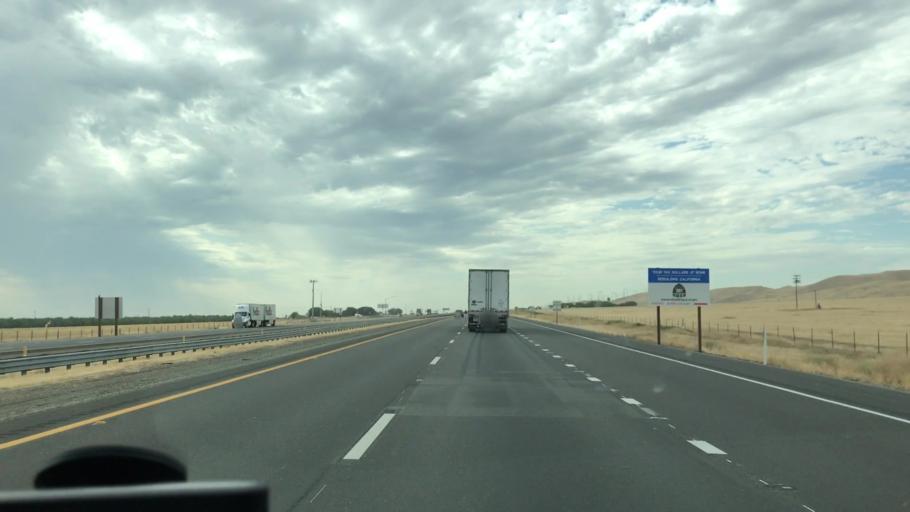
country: US
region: California
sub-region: San Joaquin County
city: Tracy
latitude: 37.5884
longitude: -121.3305
